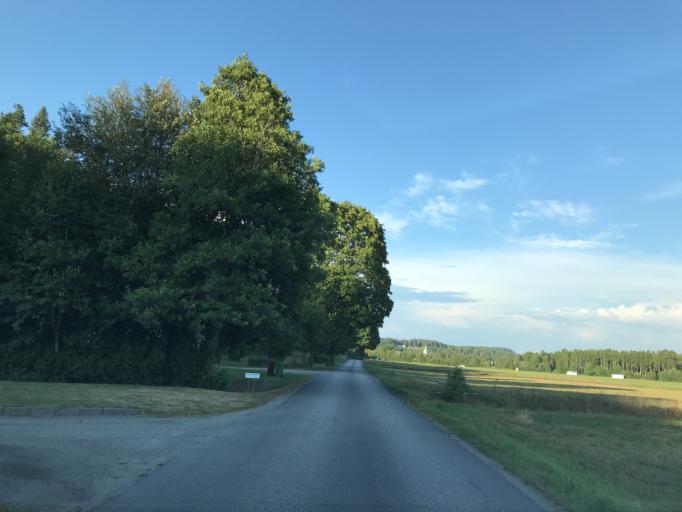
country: SE
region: Vaestra Goetaland
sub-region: Bollebygds Kommun
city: Bollebygd
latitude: 57.7908
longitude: 12.6154
